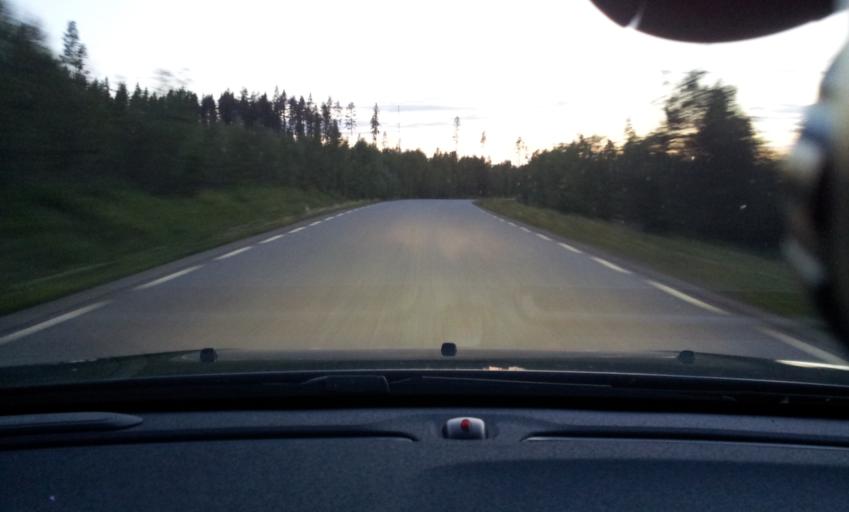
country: SE
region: Jaemtland
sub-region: Braecke Kommun
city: Braecke
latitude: 62.7356
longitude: 15.3955
